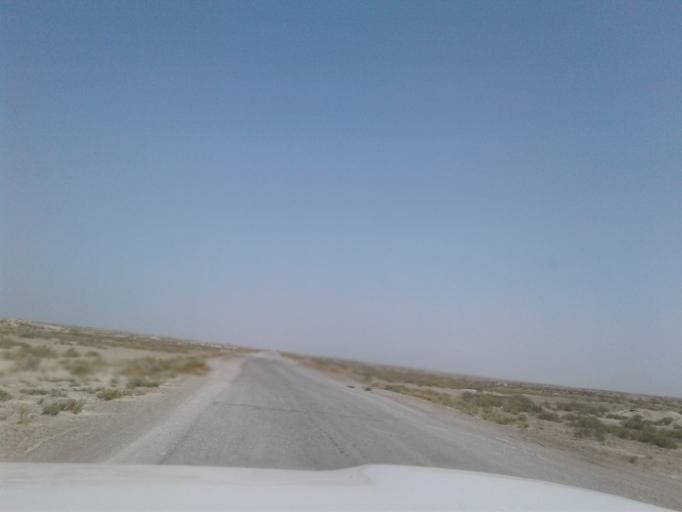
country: IR
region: Golestan
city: Gomishan
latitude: 37.9283
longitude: 53.8456
